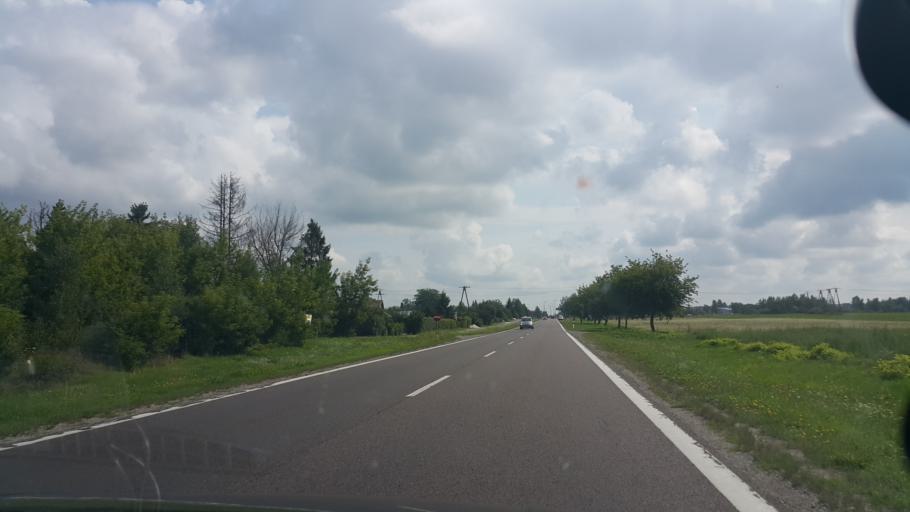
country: PL
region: Lublin Voivodeship
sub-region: Powiat wlodawski
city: Wlodawa
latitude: 51.5484
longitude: 23.5306
